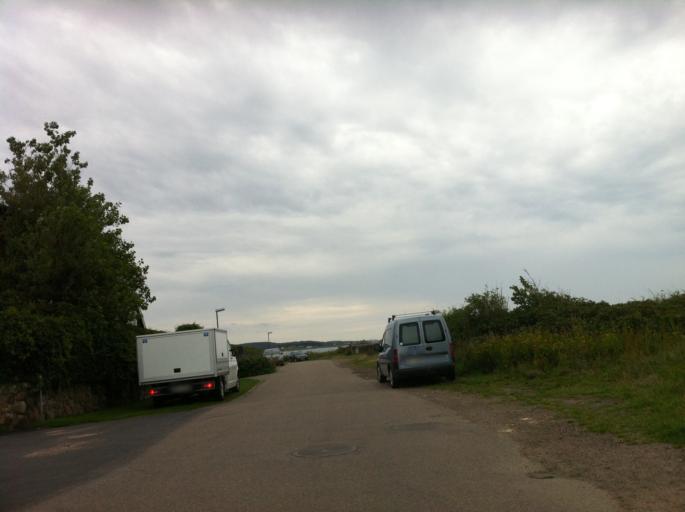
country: SE
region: Skane
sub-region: Hoganas Kommun
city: Hoganas
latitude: 56.1888
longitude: 12.5558
